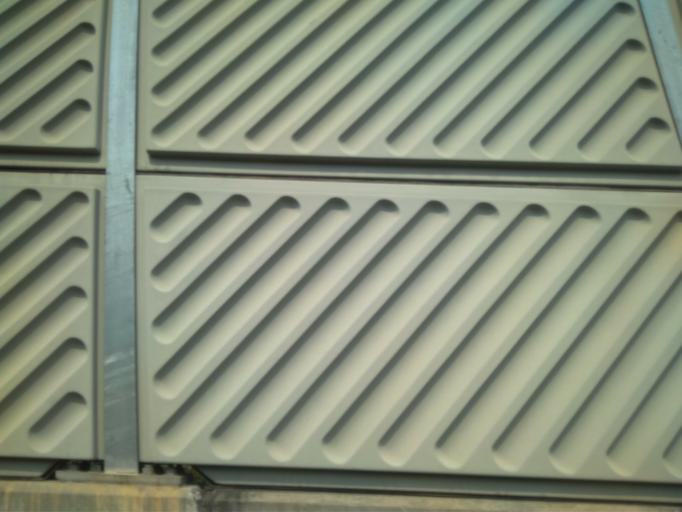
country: TH
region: Bangkok
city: Taling Chan
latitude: 13.7940
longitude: 100.4339
